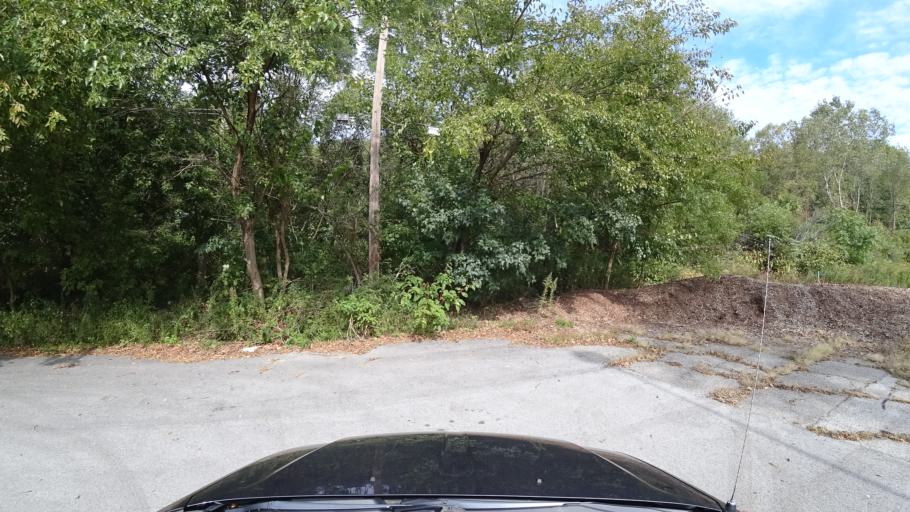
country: US
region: Indiana
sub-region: LaPorte County
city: Trail Creek
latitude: 41.7166
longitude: -86.8515
